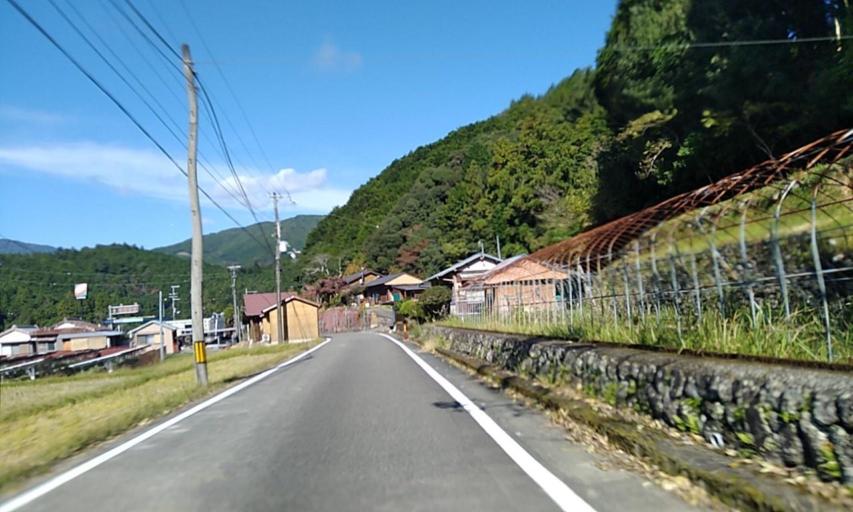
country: JP
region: Wakayama
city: Shingu
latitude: 33.9268
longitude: 135.9815
